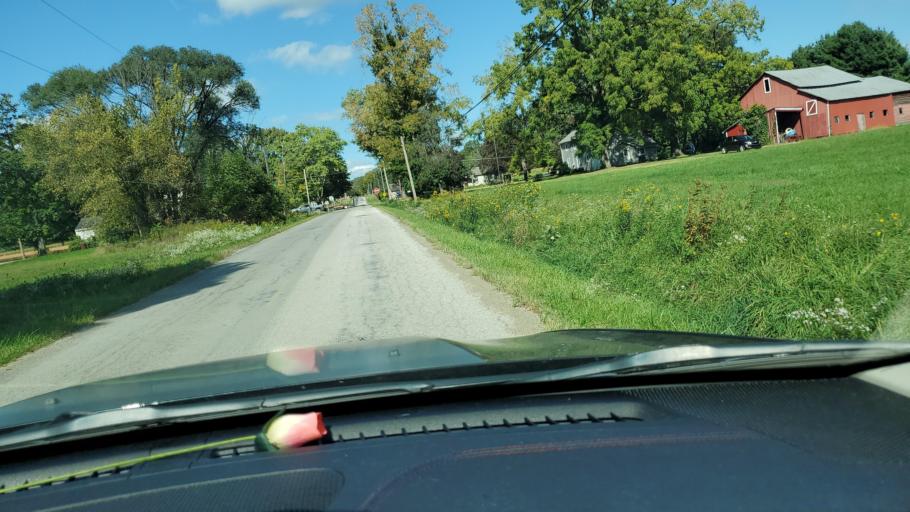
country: US
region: Ohio
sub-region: Ashtabula County
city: Andover
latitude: 41.4541
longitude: -80.5862
